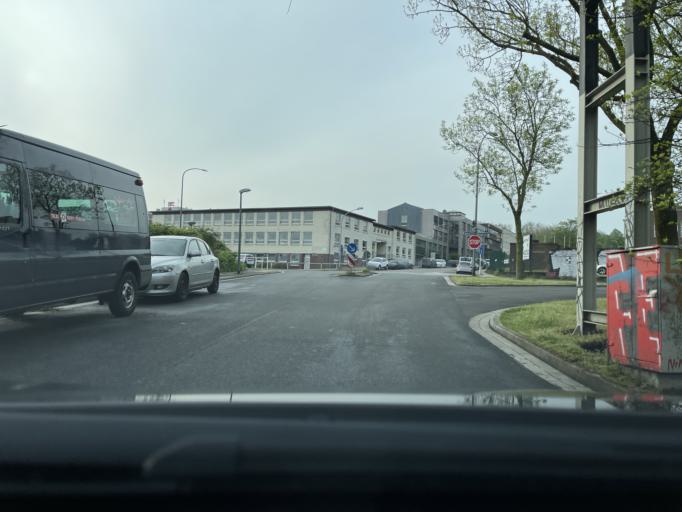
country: DE
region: North Rhine-Westphalia
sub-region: Regierungsbezirk Dusseldorf
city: Essen
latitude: 51.4478
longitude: 6.9902
